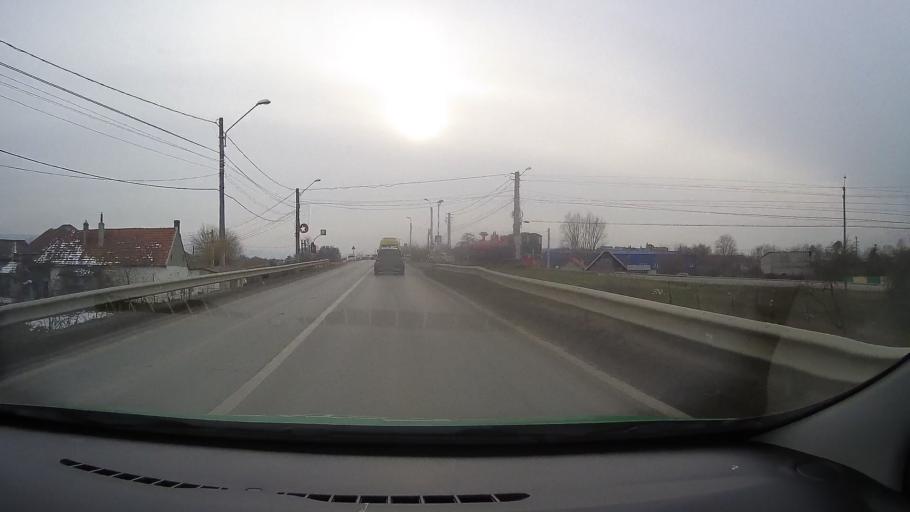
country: RO
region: Hunedoara
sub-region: Municipiul Orastie
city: Orastie
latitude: 45.8559
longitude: 23.2093
